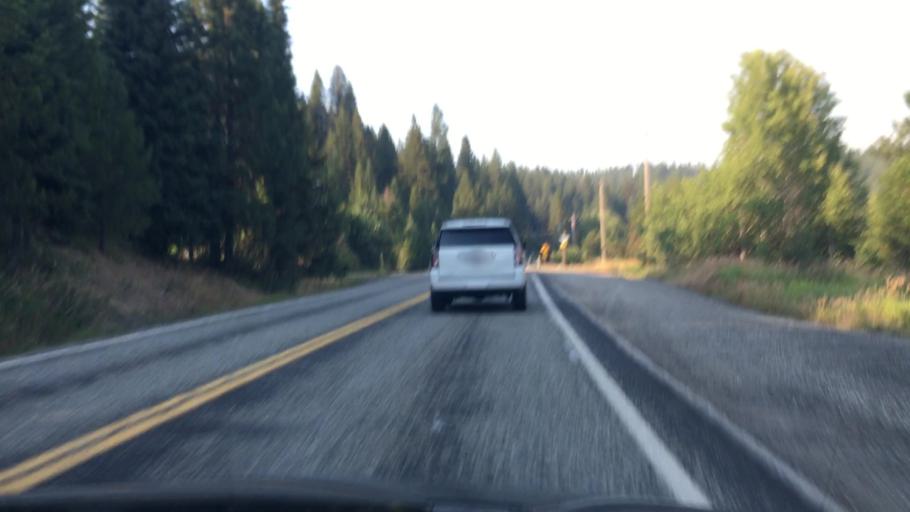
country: US
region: Idaho
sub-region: Valley County
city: Cascade
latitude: 44.3087
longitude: -116.0871
